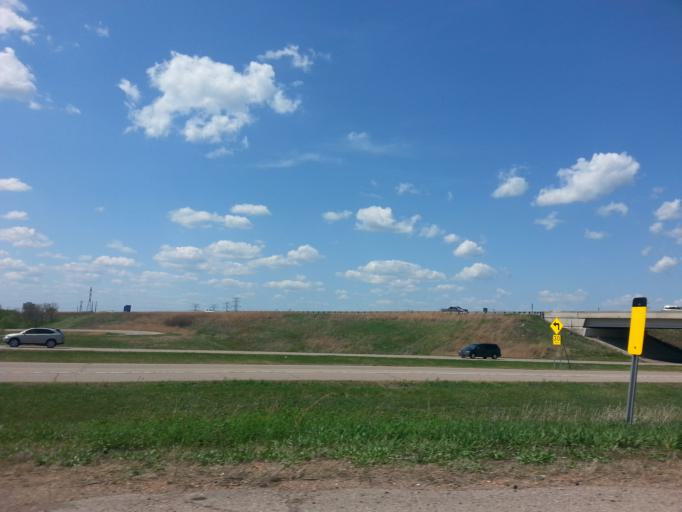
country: US
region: Minnesota
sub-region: Scott County
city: Prior Lake
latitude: 44.7850
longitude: -93.4128
